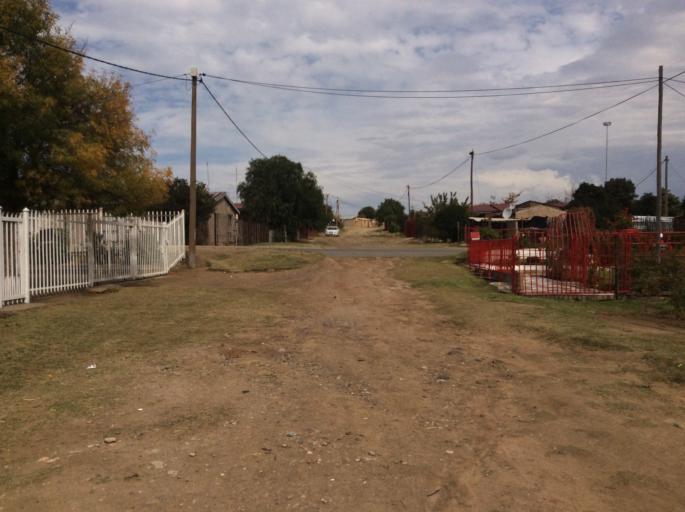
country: LS
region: Mafeteng
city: Mafeteng
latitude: -29.7192
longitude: 27.0300
